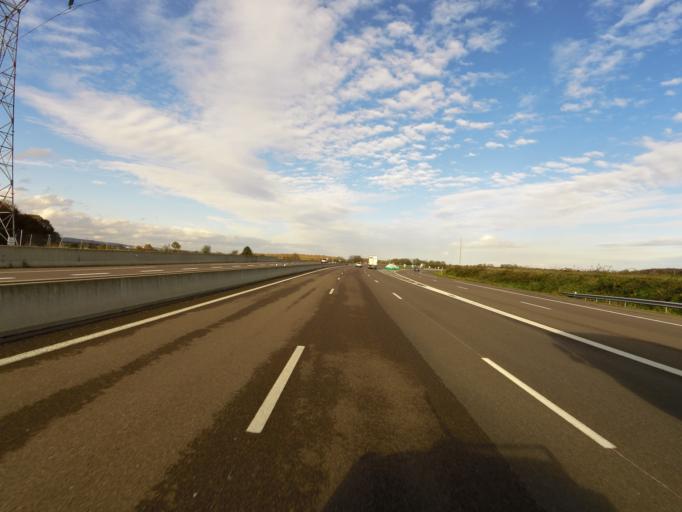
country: FR
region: Bourgogne
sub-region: Departement de la Cote-d'Or
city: Perrigny-les-Dijon
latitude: 47.2372
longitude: 5.0233
